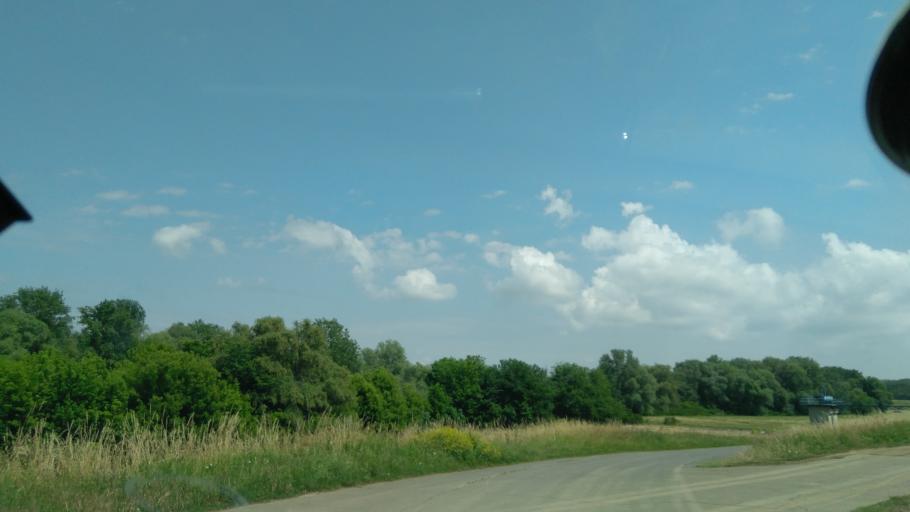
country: HU
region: Bekes
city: Bekes
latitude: 46.7642
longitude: 21.1498
